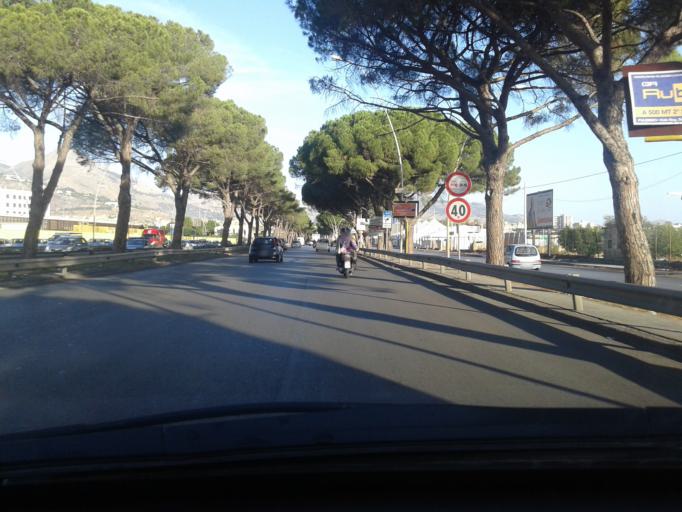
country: IT
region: Sicily
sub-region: Palermo
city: Villa Ciambra
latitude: 38.0910
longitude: 13.3432
